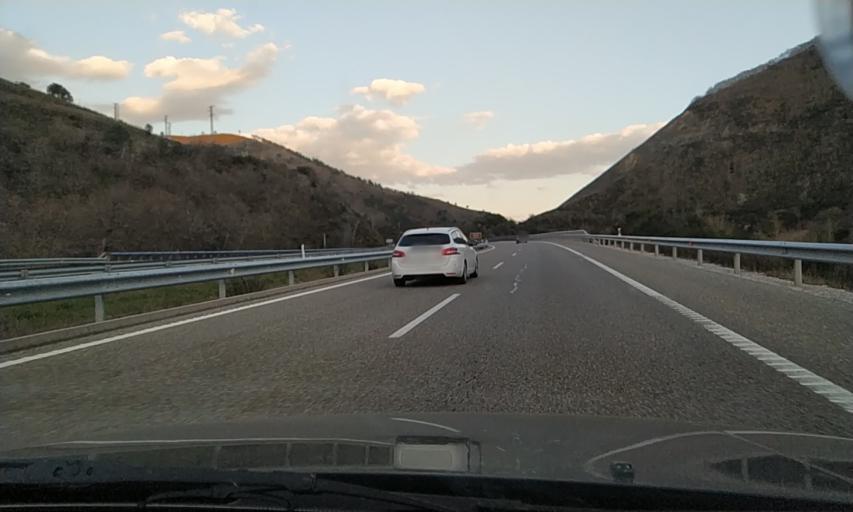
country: ES
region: Castille and Leon
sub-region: Provincia de Leon
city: Villafranca del Bierzo
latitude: 42.6230
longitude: -6.8403
